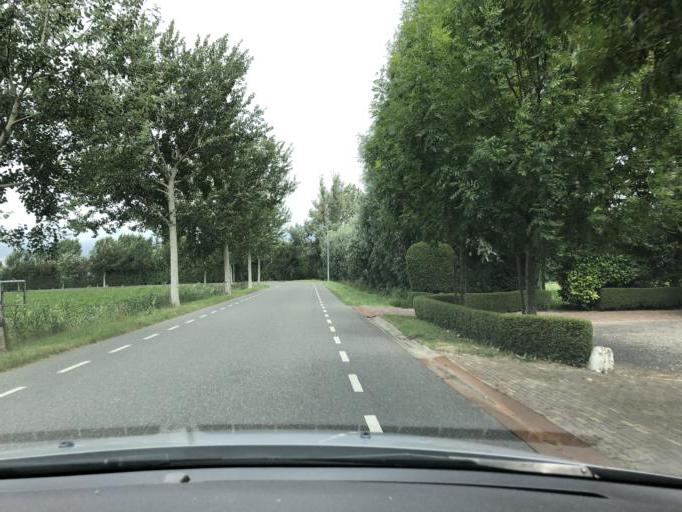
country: NL
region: Zeeland
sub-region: Gemeente Reimerswaal
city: Yerseke
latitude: 51.4299
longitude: 4.0737
